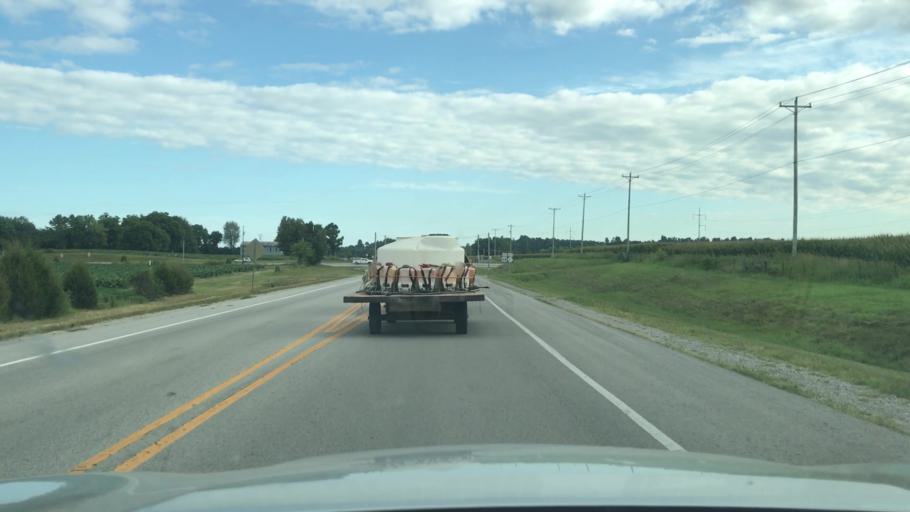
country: US
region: Kentucky
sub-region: Todd County
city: Elkton
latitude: 36.8218
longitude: -87.1510
